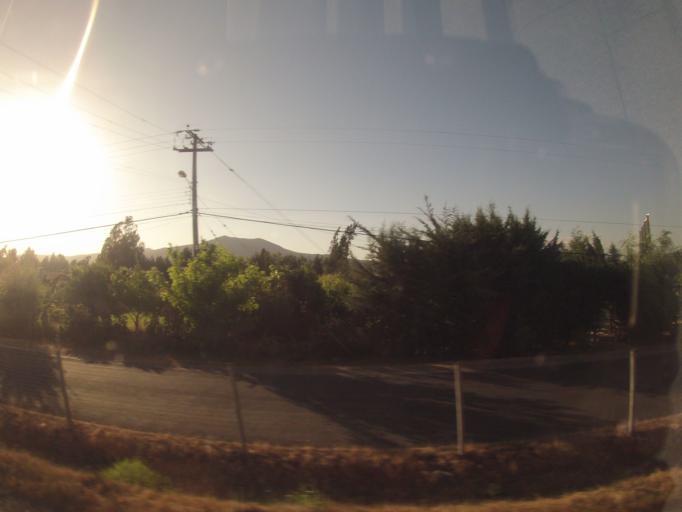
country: CL
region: O'Higgins
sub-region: Provincia de Colchagua
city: Chimbarongo
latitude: -34.6876
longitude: -71.0129
